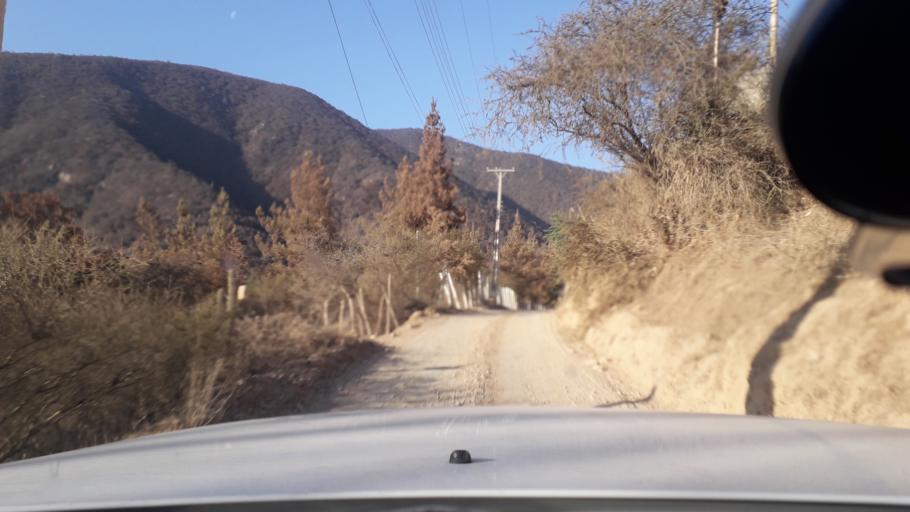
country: CL
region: Valparaiso
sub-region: Provincia de Marga Marga
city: Limache
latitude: -33.0524
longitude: -71.0883
